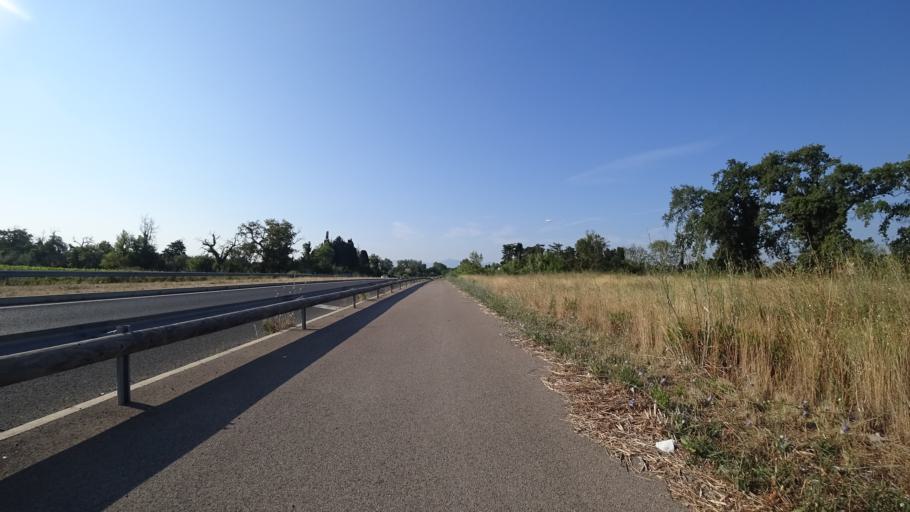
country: FR
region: Languedoc-Roussillon
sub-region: Departement des Pyrenees-Orientales
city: Perpignan
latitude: 42.7217
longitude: 2.9028
